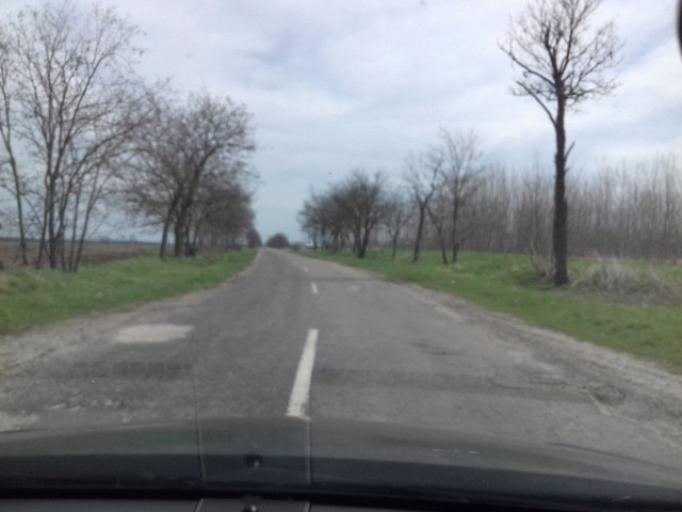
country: HU
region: Jasz-Nagykun-Szolnok
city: Cserkeszolo
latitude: 46.9029
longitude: 20.1634
